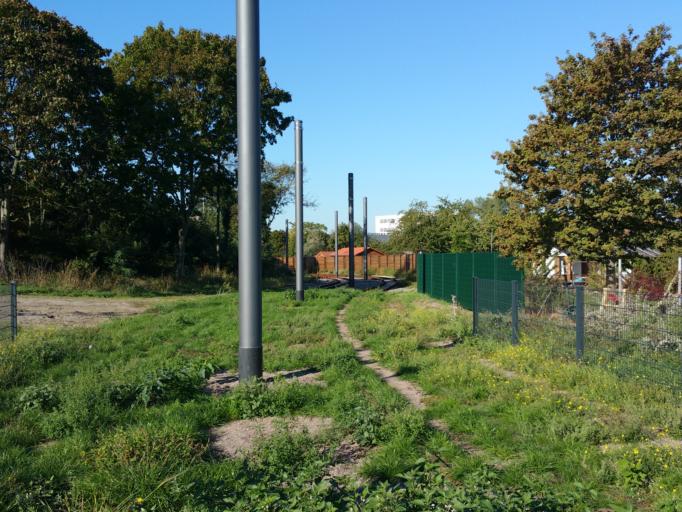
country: DE
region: Baden-Wuerttemberg
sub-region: Karlsruhe Region
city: Mannheim
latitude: 49.5132
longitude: 8.4947
